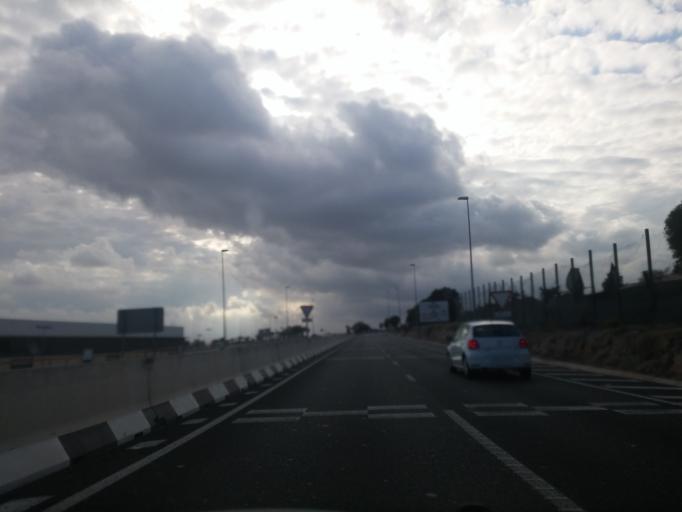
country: ES
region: Valencia
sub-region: Provincia de Alicante
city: Alicante
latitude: 38.2967
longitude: -0.5744
